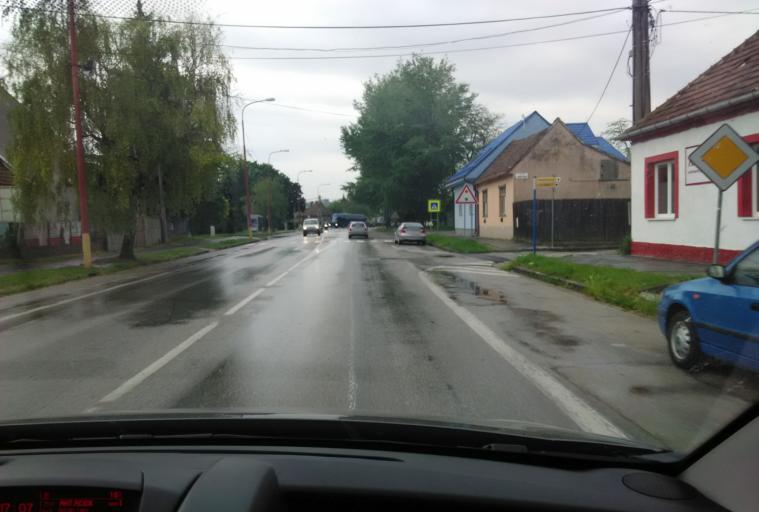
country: SK
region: Trnavsky
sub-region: Okres Trnava
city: Trnava
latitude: 48.3923
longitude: 17.5963
